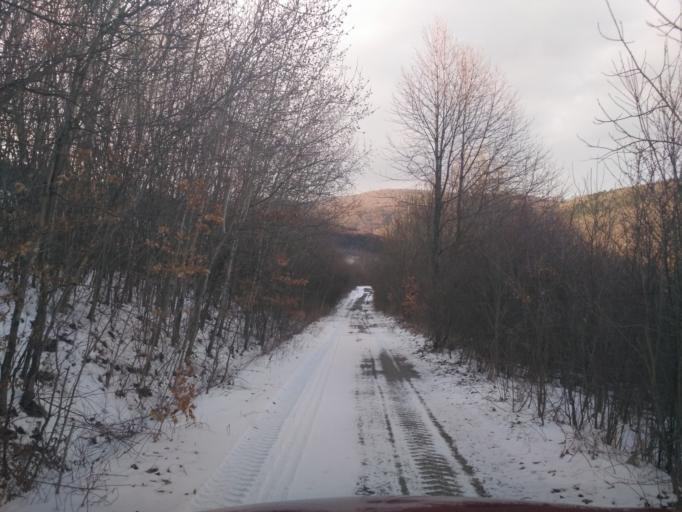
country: SK
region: Kosicky
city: Kosice
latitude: 48.7387
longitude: 21.1506
